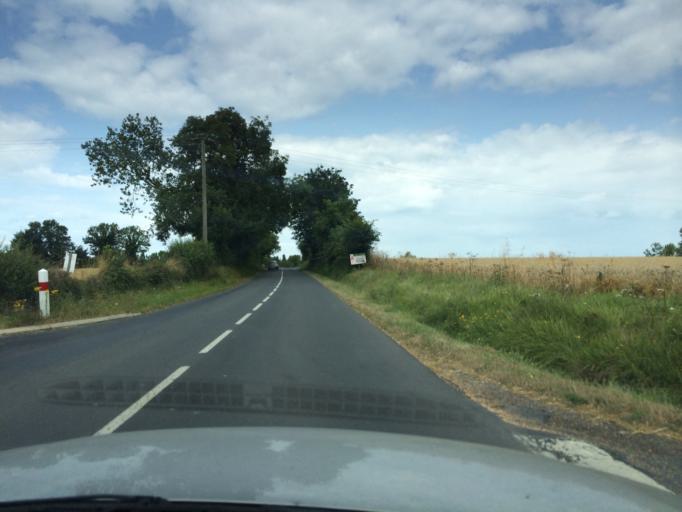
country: FR
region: Lower Normandy
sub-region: Departement du Calvados
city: Saint-Vigor-le-Grand
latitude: 49.2989
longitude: -0.6861
